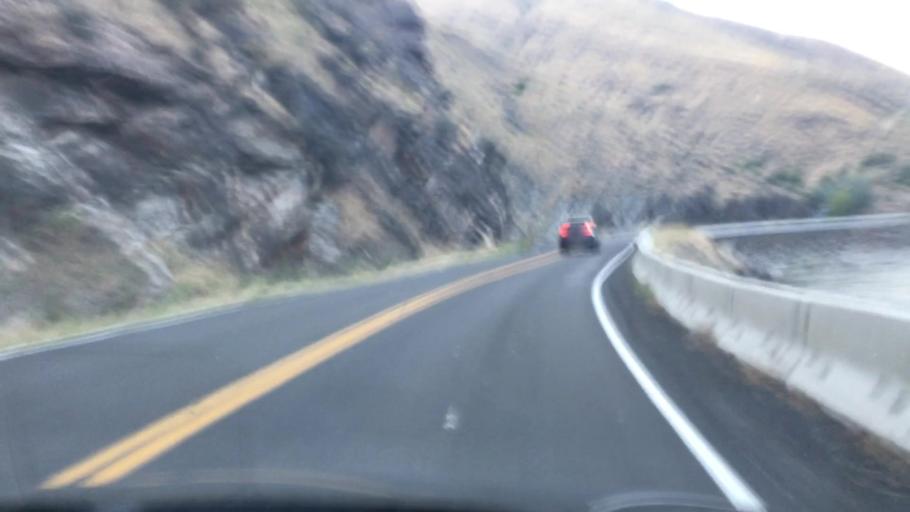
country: US
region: Idaho
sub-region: Idaho County
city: Grangeville
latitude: 45.4347
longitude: -116.3195
